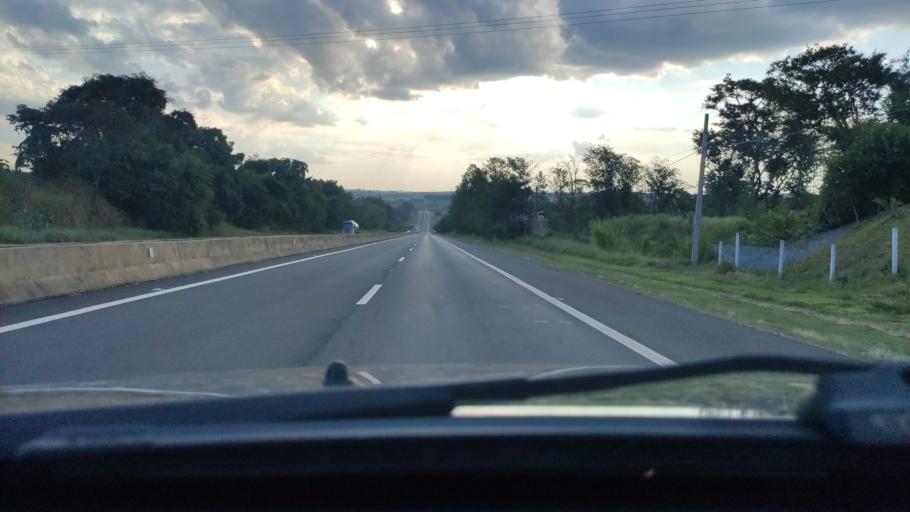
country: BR
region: Sao Paulo
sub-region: Mogi-Mirim
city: Mogi Mirim
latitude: -22.4439
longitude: -47.0325
